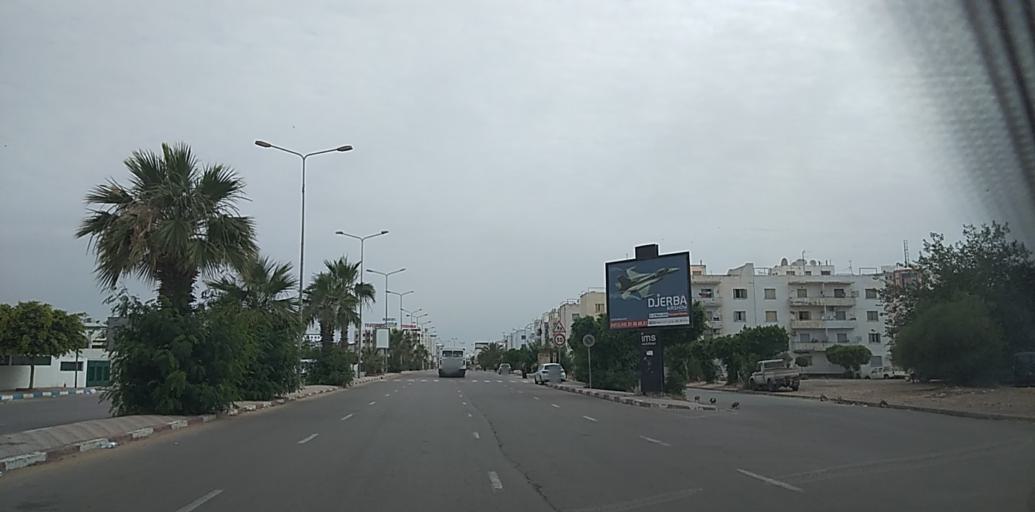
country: TN
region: Safaqis
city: Sfax
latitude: 34.7413
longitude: 10.7596
